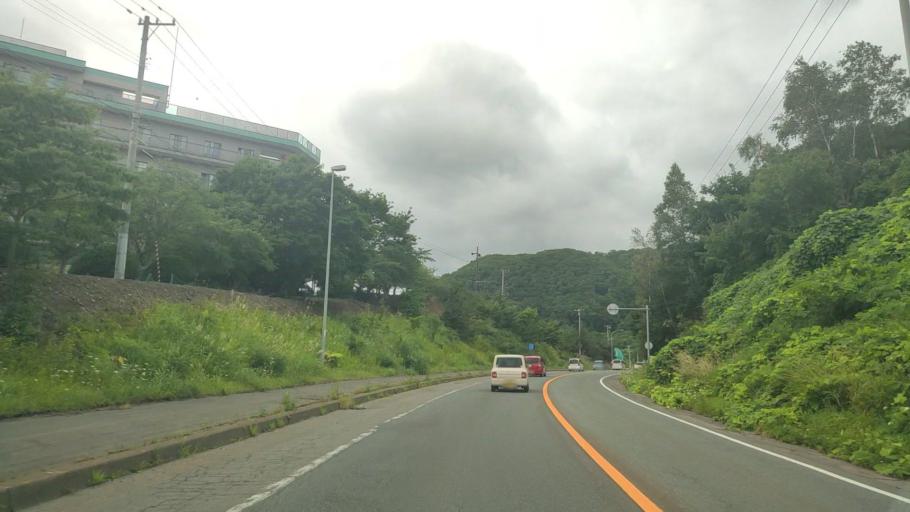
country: JP
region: Hokkaido
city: Date
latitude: 42.5584
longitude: 140.7470
